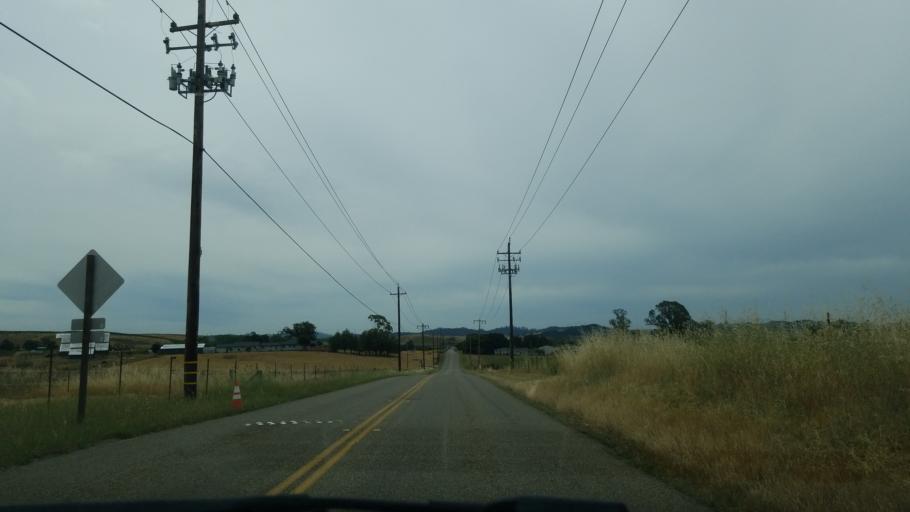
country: US
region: California
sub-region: San Luis Obispo County
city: San Luis Obispo
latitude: 35.2266
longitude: -120.5996
